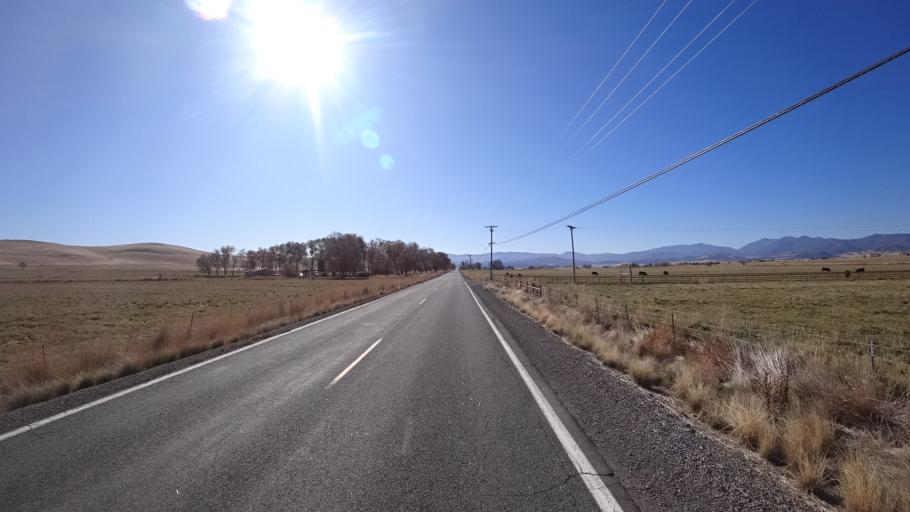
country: US
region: California
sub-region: Siskiyou County
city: Montague
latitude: 41.7467
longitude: -122.5047
